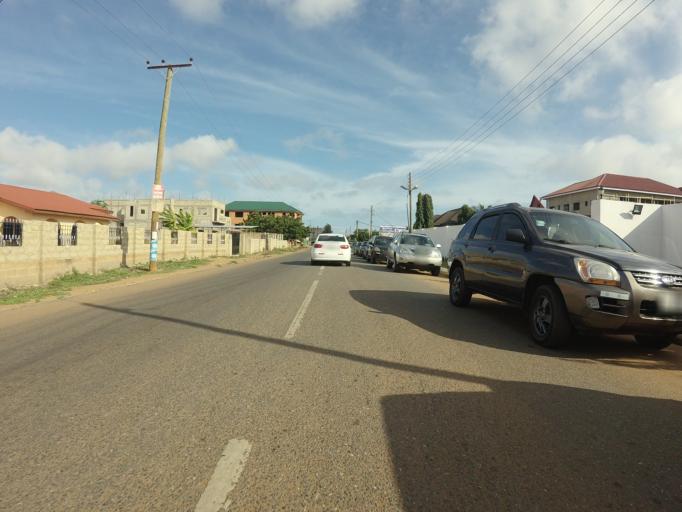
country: GH
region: Greater Accra
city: Teshi Old Town
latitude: 5.5840
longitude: -0.1425
